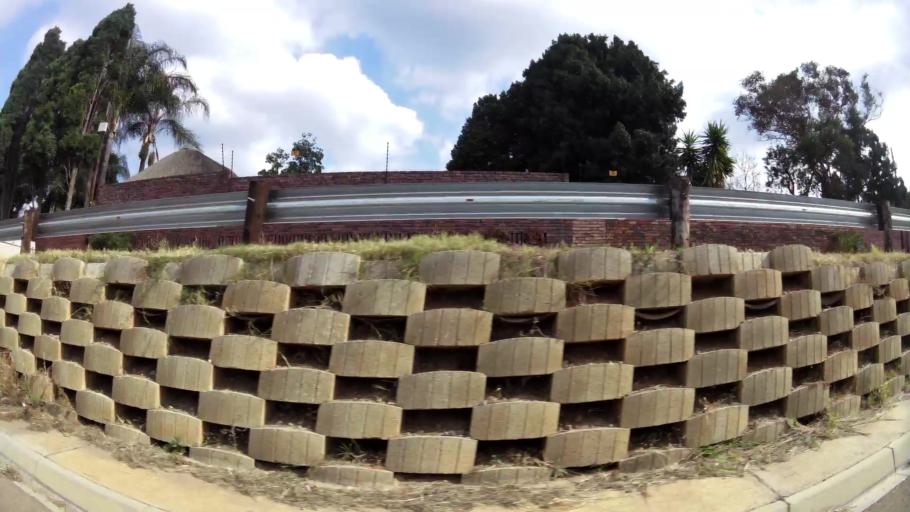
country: ZA
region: Gauteng
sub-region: City of Tshwane Metropolitan Municipality
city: Pretoria
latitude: -25.7596
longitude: 28.3231
